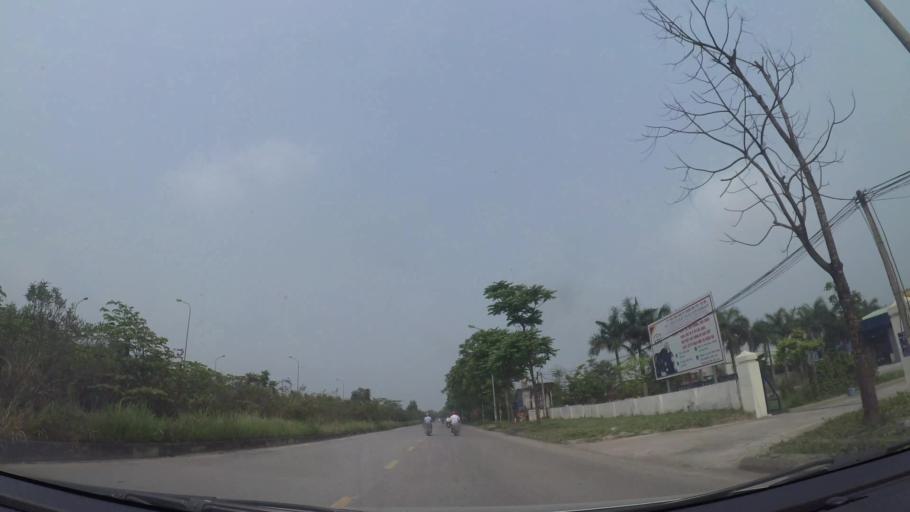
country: VN
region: Ha Noi
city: Quoc Oai
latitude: 21.0016
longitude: 105.6056
